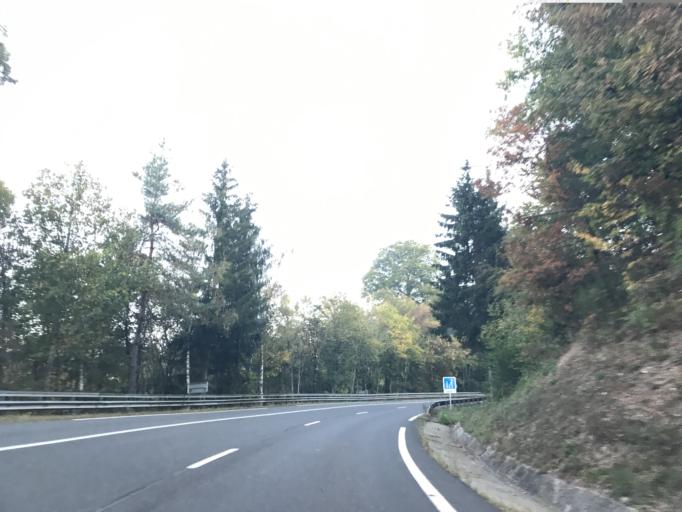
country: FR
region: Auvergne
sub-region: Departement du Puy-de-Dome
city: Celles-sur-Durolle
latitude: 45.8725
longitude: 3.6263
